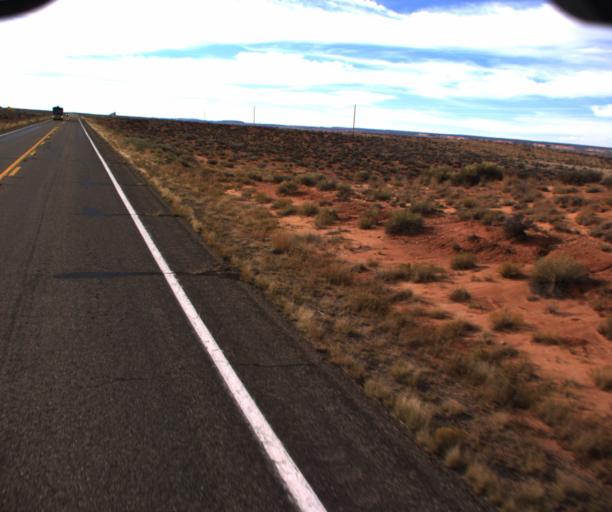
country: US
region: Arizona
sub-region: Coconino County
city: LeChee
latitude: 36.7573
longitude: -111.2851
